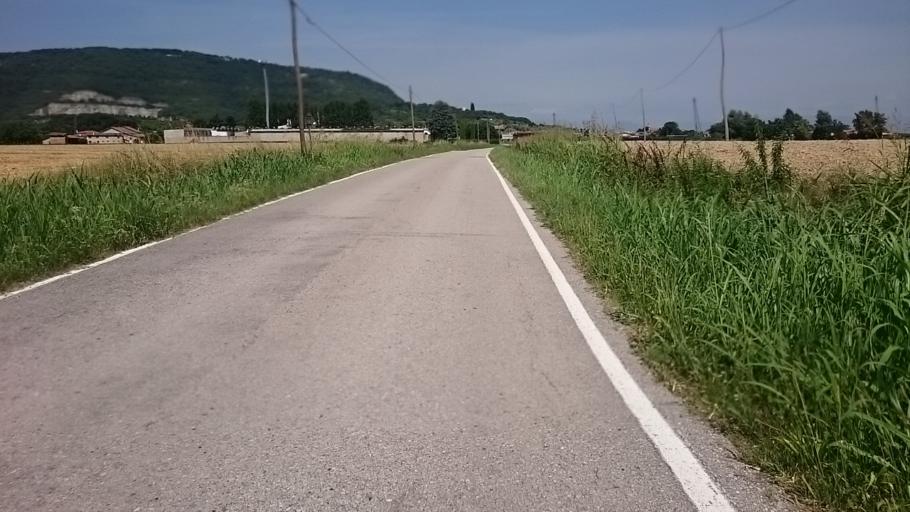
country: IT
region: Veneto
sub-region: Provincia di Vicenza
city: Longare
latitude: 45.4656
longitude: 11.6171
